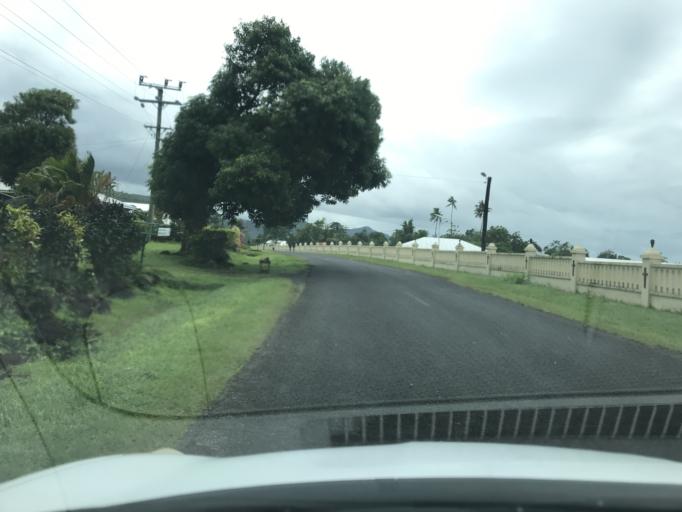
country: WS
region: Atua
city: Lufilufi
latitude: -13.8751
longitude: -171.5973
